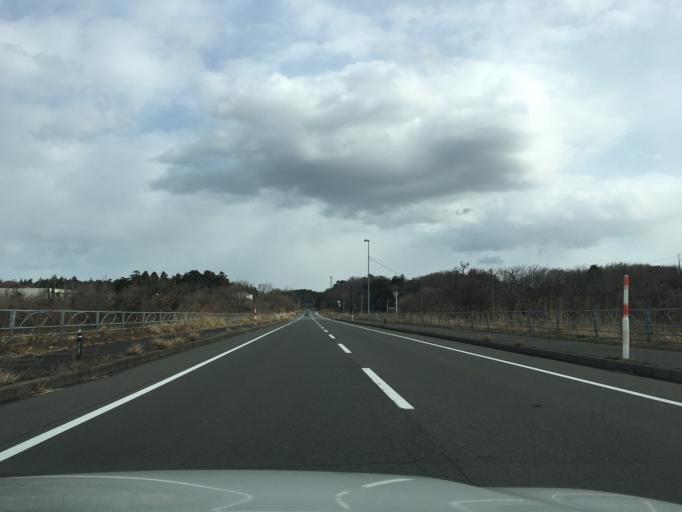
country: JP
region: Yamagata
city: Yuza
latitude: 39.2450
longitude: 139.9218
